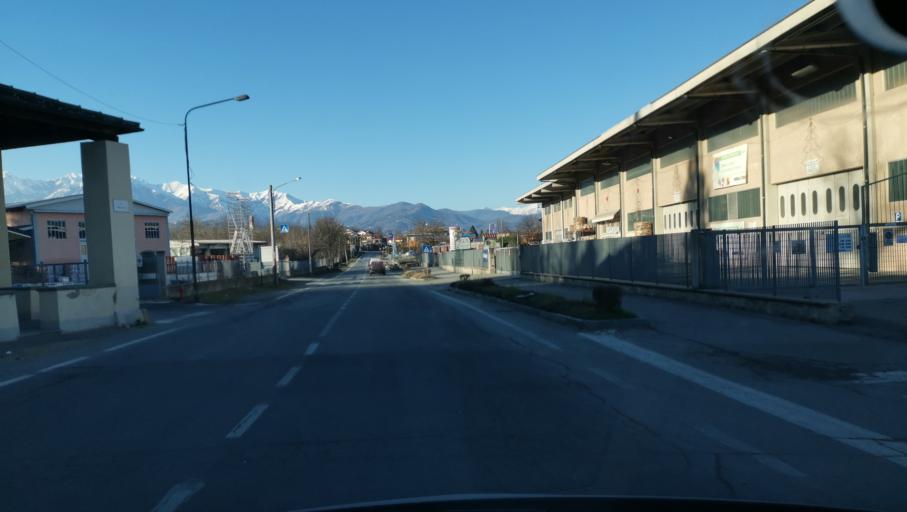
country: IT
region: Piedmont
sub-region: Provincia di Cuneo
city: Bagnolo Piemonte
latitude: 44.7655
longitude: 7.3114
